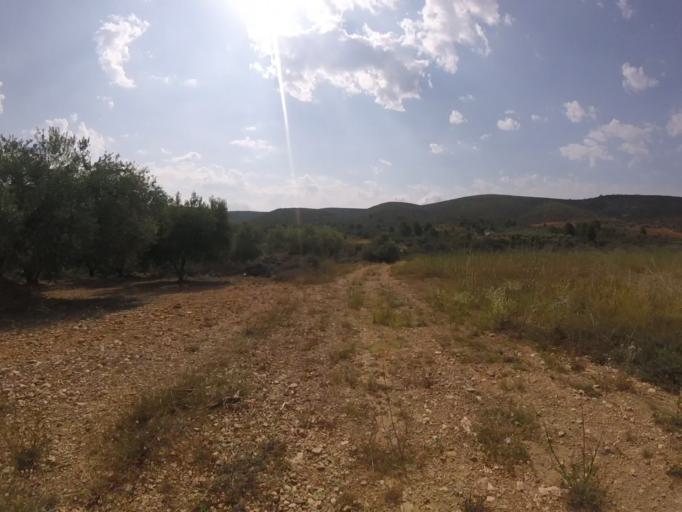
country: ES
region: Valencia
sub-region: Provincia de Castello
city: Alcala de Xivert
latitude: 40.3367
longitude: 0.1974
